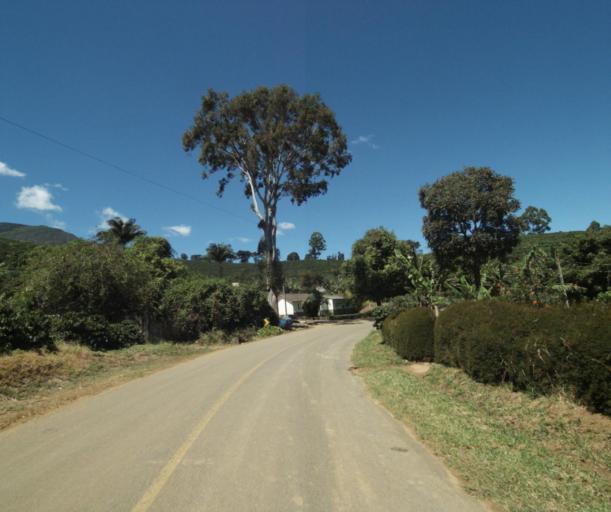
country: BR
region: Minas Gerais
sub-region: Espera Feliz
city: Espera Feliz
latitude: -20.5670
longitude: -41.8277
